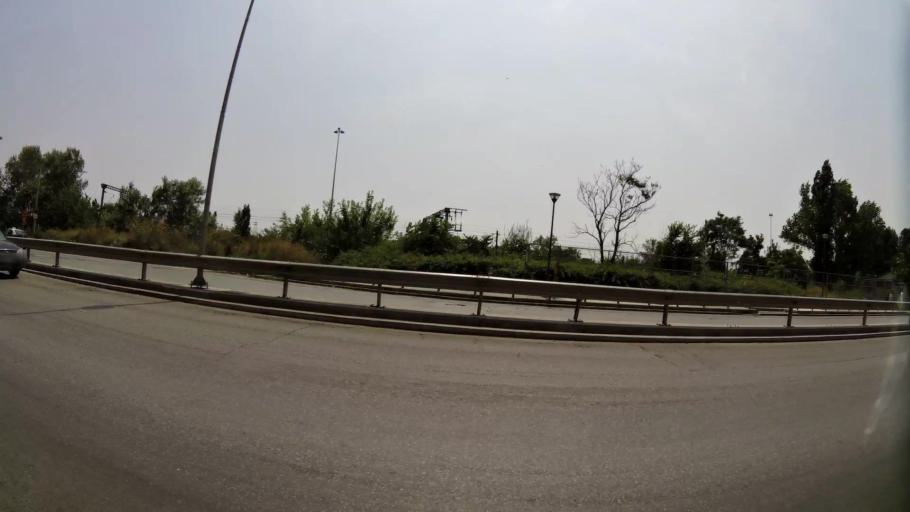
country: GR
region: Central Macedonia
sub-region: Nomos Thessalonikis
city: Menemeni
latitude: 40.6638
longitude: 22.8962
